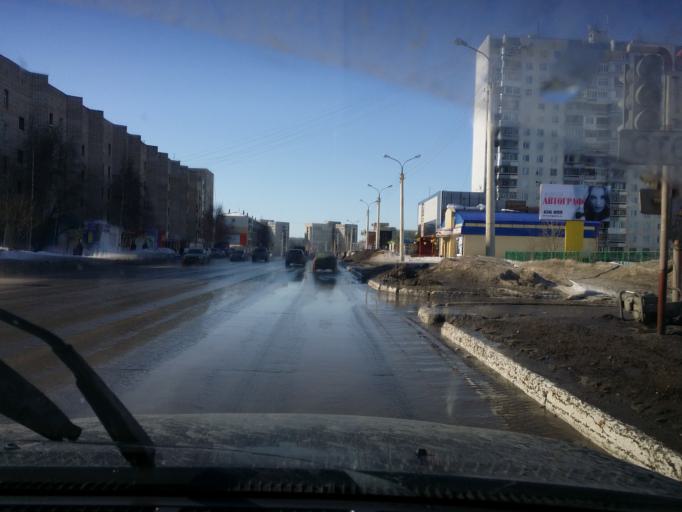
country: RU
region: Khanty-Mansiyskiy Avtonomnyy Okrug
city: Nizhnevartovsk
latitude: 60.9442
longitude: 76.5745
